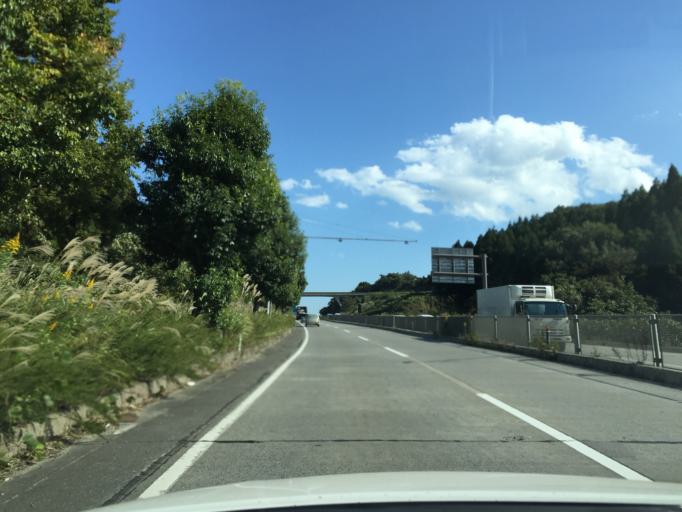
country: JP
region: Fukushima
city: Iwaki
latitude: 37.0236
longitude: 140.8855
